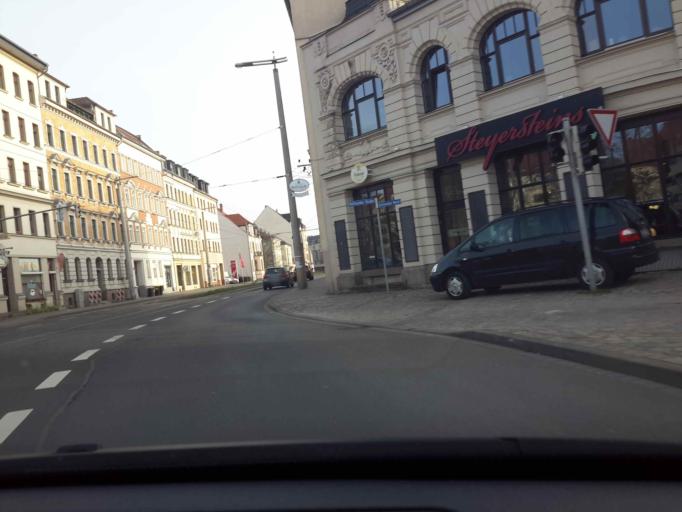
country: DE
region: Saxony
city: Leipzig
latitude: 51.3680
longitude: 12.3858
